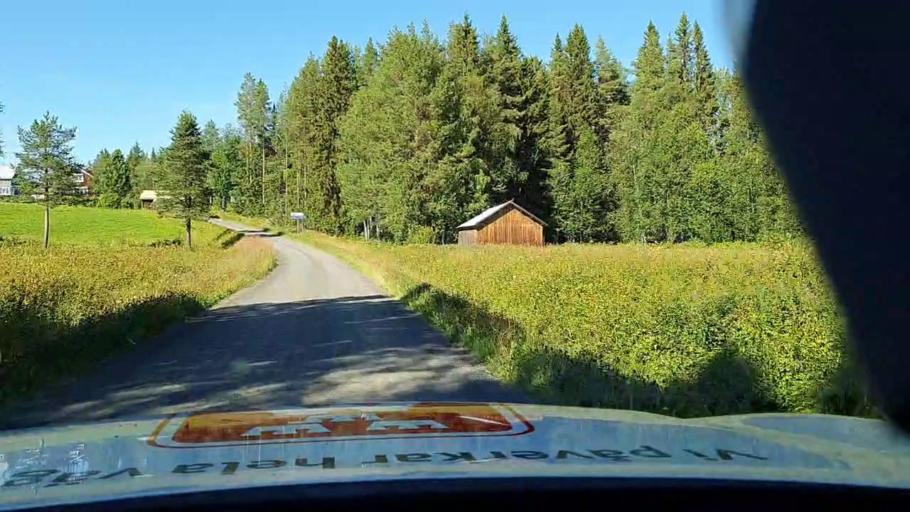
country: SE
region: Jaemtland
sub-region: OEstersunds Kommun
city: Lit
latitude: 63.7722
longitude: 14.6550
